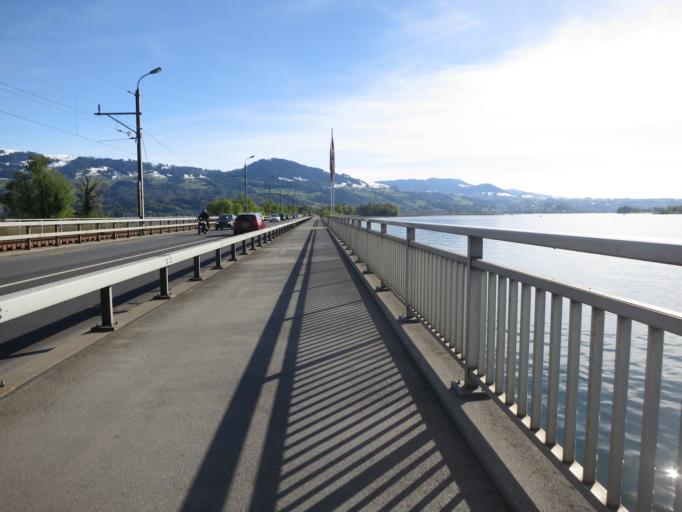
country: CH
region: Saint Gallen
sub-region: Wahlkreis See-Gaster
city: Rapperswil
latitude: 47.2243
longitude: 8.8120
